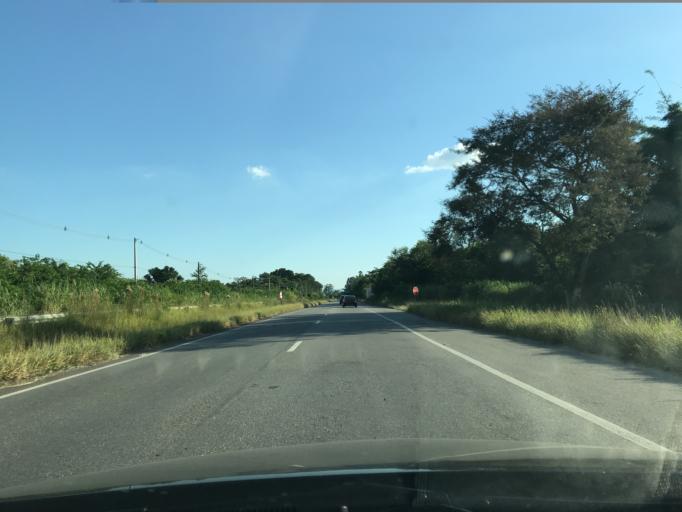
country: BR
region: Sao Paulo
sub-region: Taubate
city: Taubate
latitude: -23.0049
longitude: -45.6396
